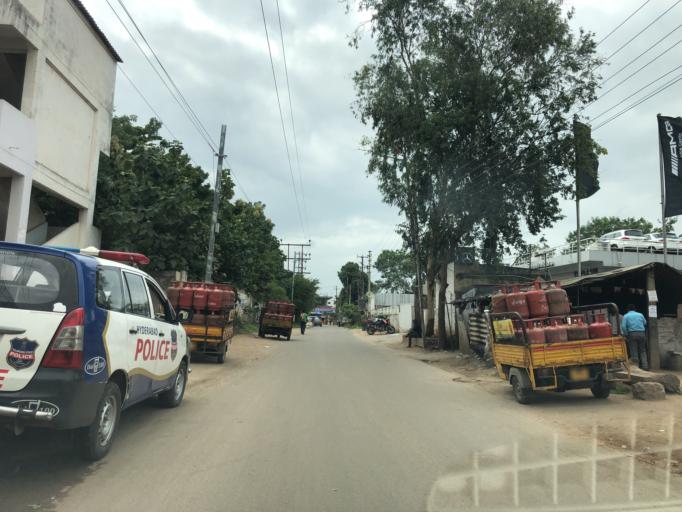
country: IN
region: Telangana
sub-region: Rangareddi
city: Quthbullapur
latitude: 17.4802
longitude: 78.4749
